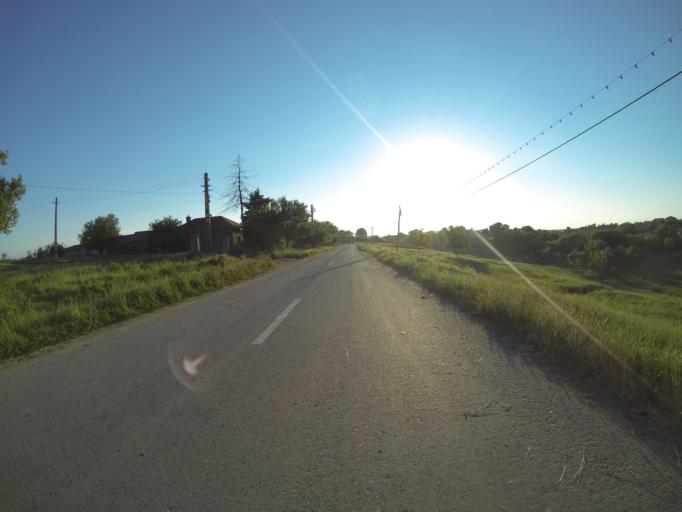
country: RO
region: Dolj
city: Satu Nou Calopar
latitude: 44.1621
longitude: 23.7683
